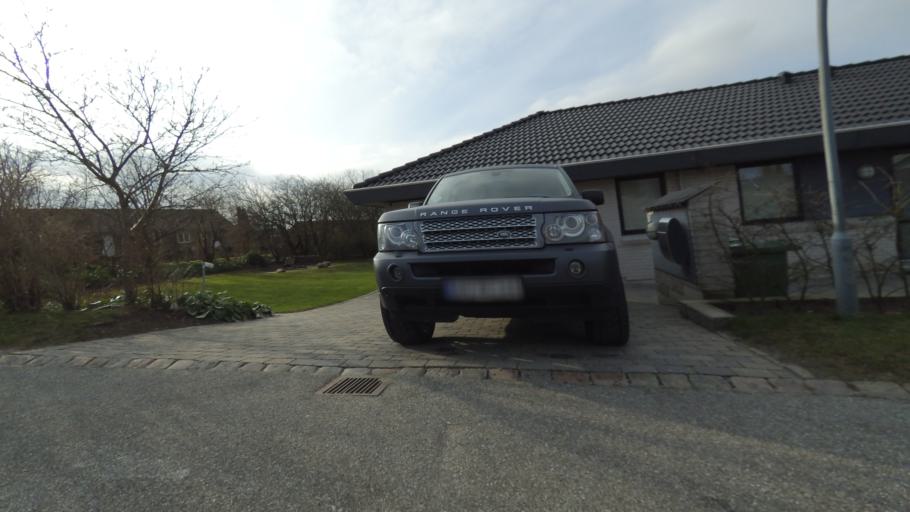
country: DK
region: Central Jutland
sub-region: Arhus Kommune
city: Kolt
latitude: 56.1091
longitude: 10.0829
